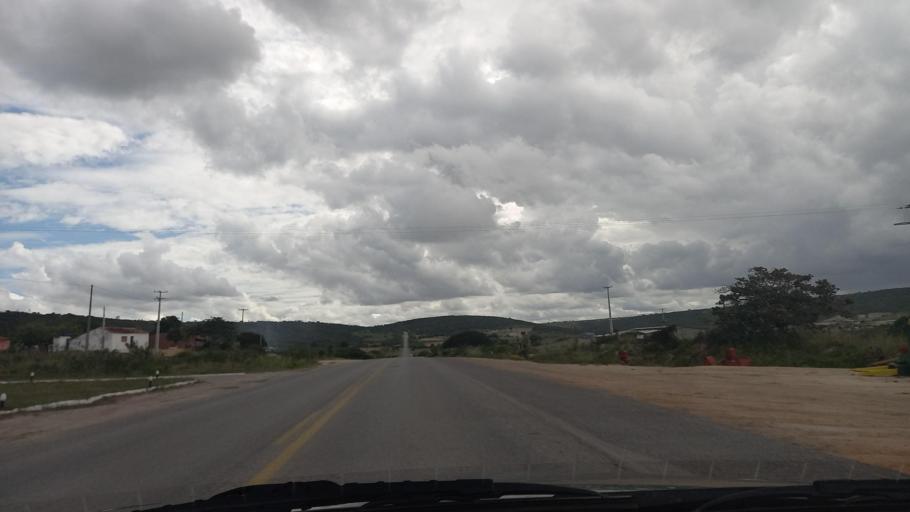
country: BR
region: Pernambuco
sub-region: Lajedo
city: Lajedo
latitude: -8.6694
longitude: -36.3791
